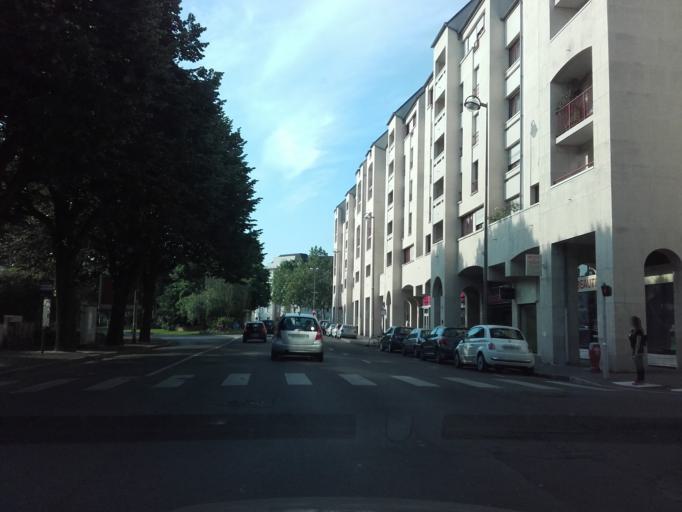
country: FR
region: Centre
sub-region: Departement d'Indre-et-Loire
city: La Riche
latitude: 47.3896
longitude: 0.6749
